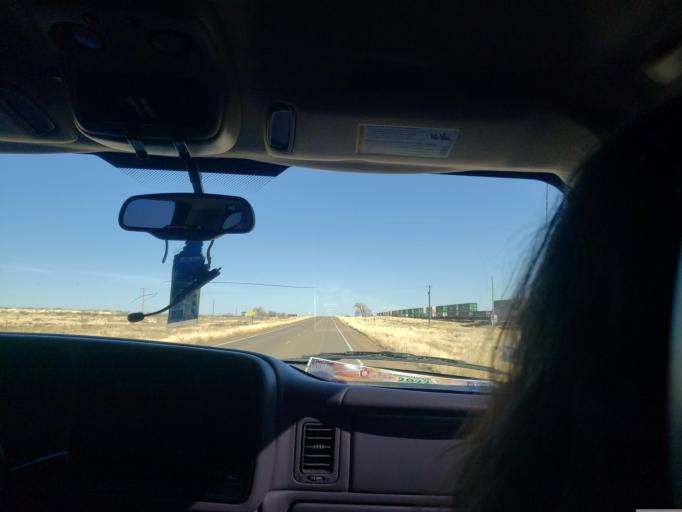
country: US
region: New Mexico
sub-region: Quay County
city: Tucumcari
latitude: 35.2062
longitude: -103.6524
